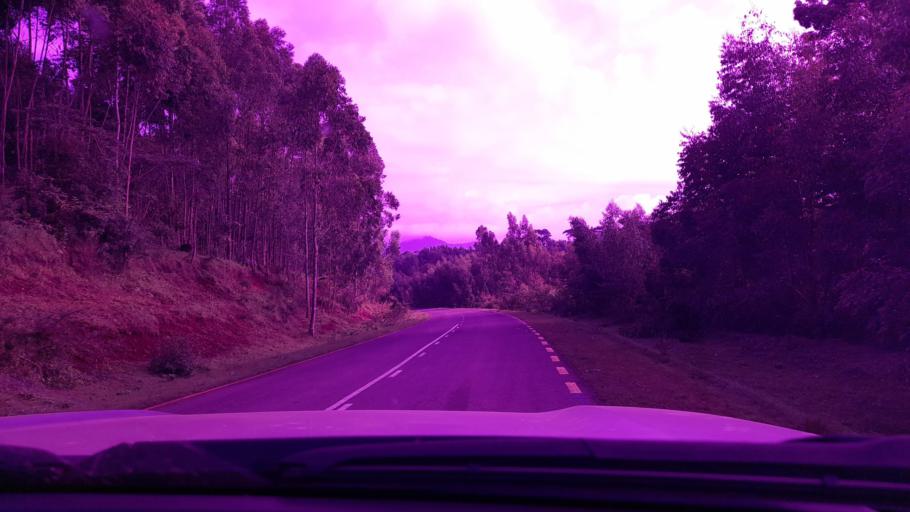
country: ET
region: Oromiya
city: Bedele
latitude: 8.1961
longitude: 36.4438
